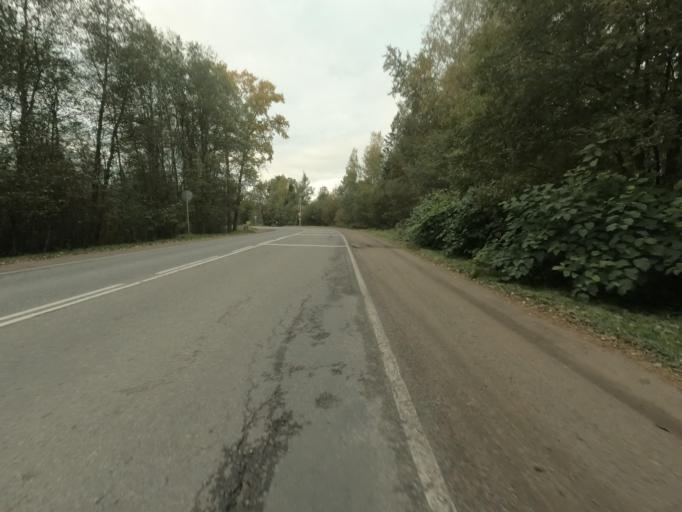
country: RU
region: Leningrad
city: Pavlovo
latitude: 59.7854
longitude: 30.9697
